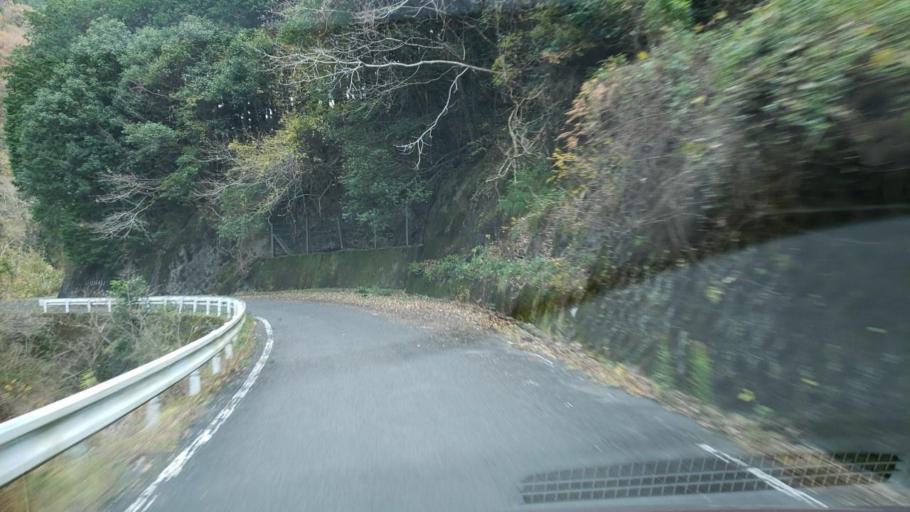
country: JP
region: Tokushima
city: Wakimachi
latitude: 34.1413
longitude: 134.2305
